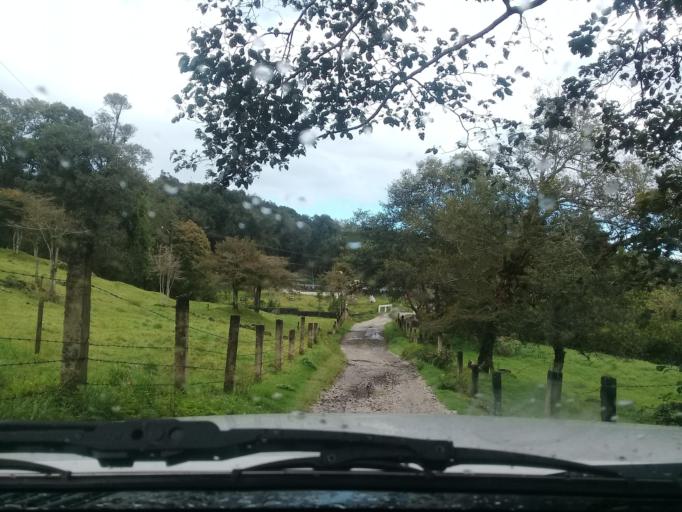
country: MX
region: Veracruz
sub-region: Acajete
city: La Joya
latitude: 19.6178
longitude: -97.0012
